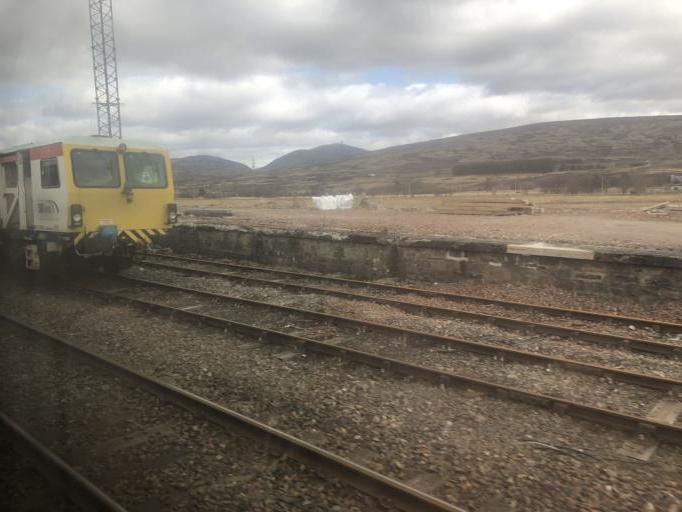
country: GB
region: Scotland
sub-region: Highland
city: Kingussie
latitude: 56.9365
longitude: -4.2454
